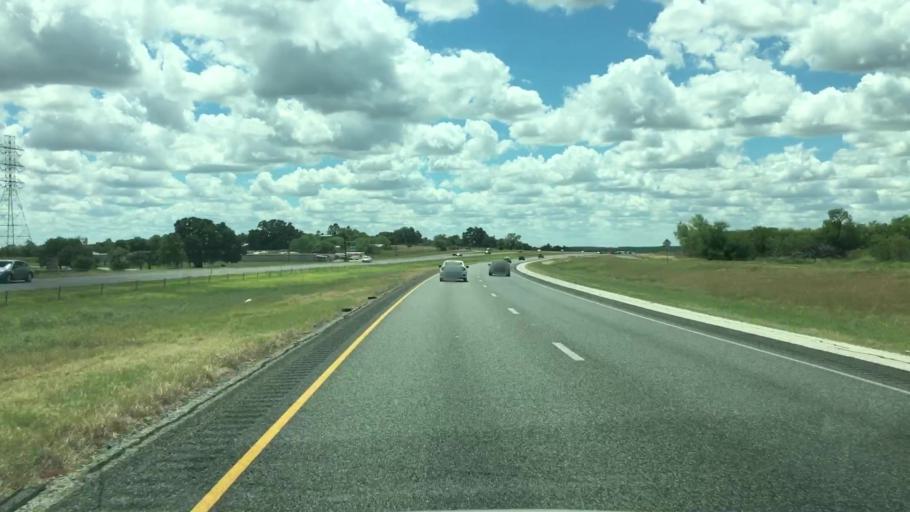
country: US
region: Texas
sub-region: Bexar County
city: Elmendorf
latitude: 29.2498
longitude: -98.3954
